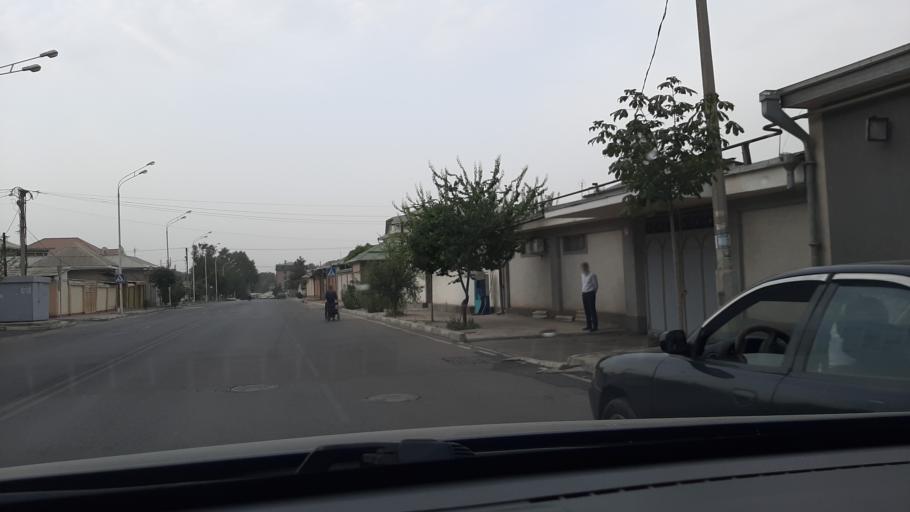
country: TJ
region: Dushanbe
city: Dushanbe
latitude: 38.6104
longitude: 68.7825
